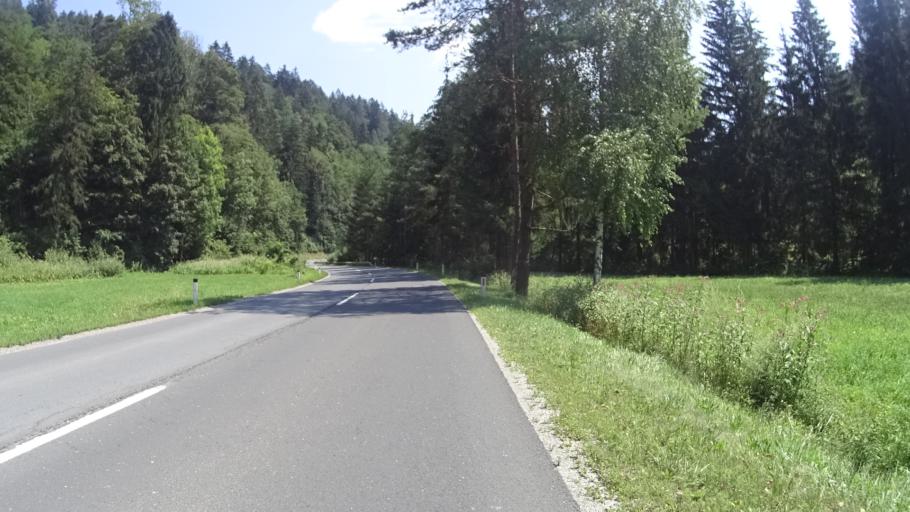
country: SI
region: Prevalje
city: Prevalje
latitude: 46.5464
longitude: 14.8992
